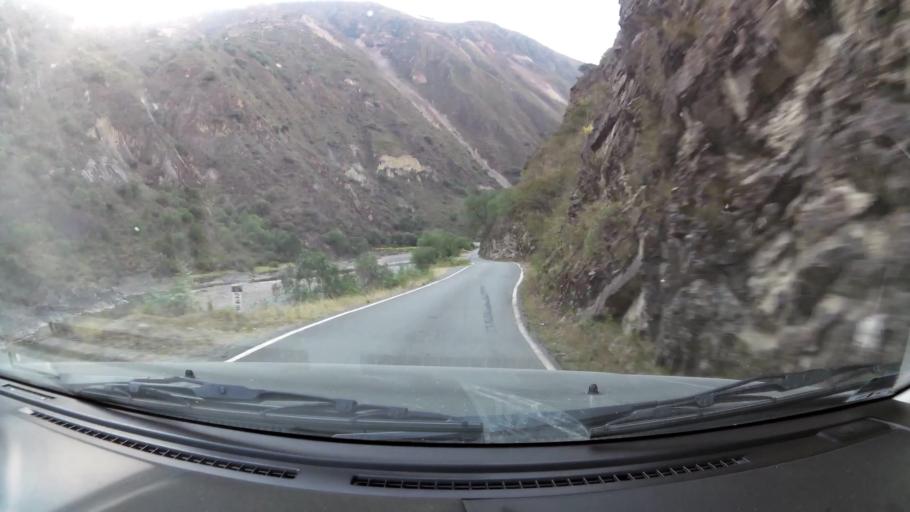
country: PE
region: Huancavelica
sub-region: Provincia de Churcampa
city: La Esmeralda
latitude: -12.5588
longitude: -74.7092
